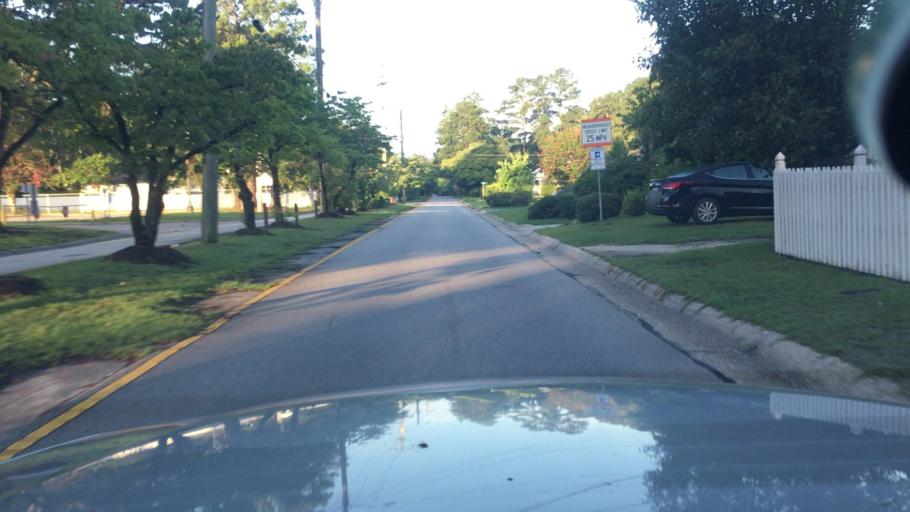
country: US
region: North Carolina
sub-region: Cumberland County
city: Fayetteville
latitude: 35.0662
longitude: -78.9168
